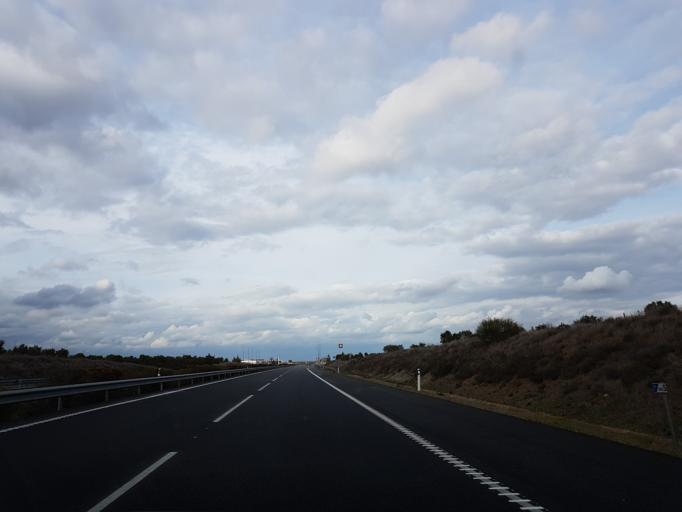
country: PT
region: Beja
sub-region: Aljustrel
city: Aljustrel
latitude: 37.9181
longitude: -8.2425
